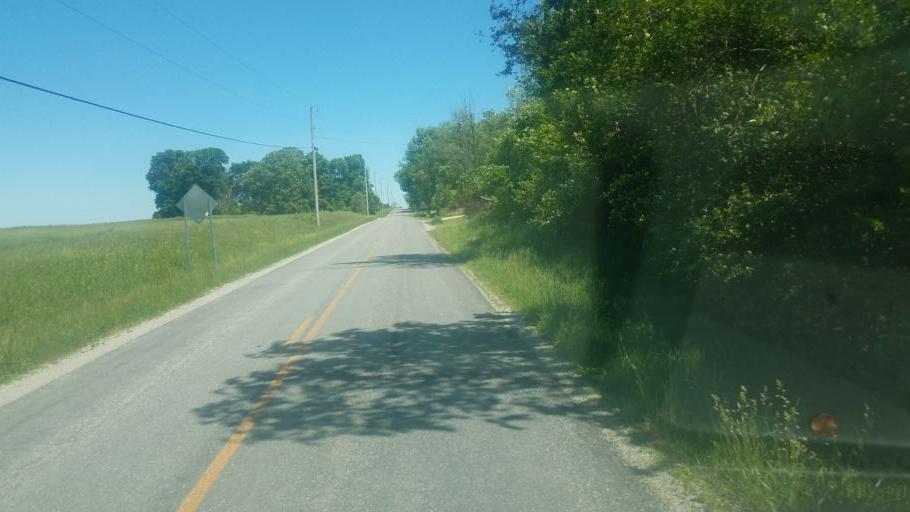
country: US
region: Ohio
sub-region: Shelby County
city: Sidney
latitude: 40.2140
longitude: -84.1613
